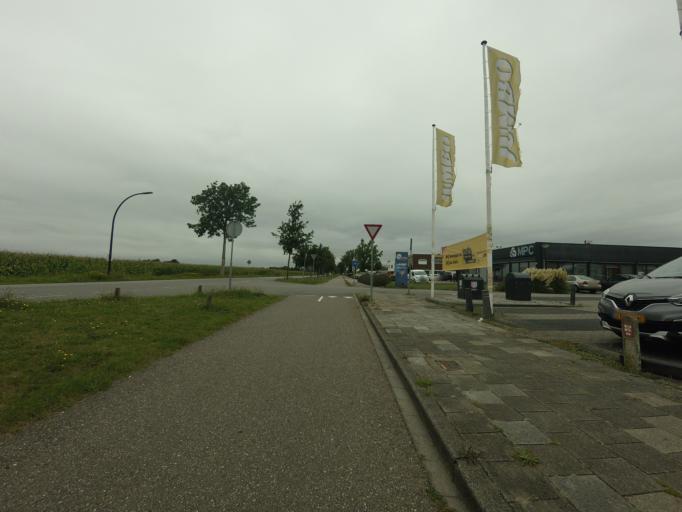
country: NL
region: Friesland
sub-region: Gemeente Opsterland
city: Gorredijk
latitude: 53.0033
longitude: 6.0565
